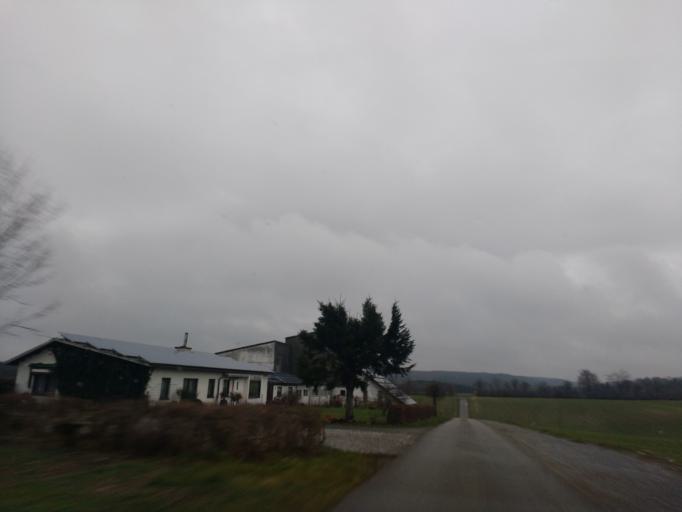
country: DE
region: North Rhine-Westphalia
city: Marsberg
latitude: 51.5451
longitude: 8.8339
